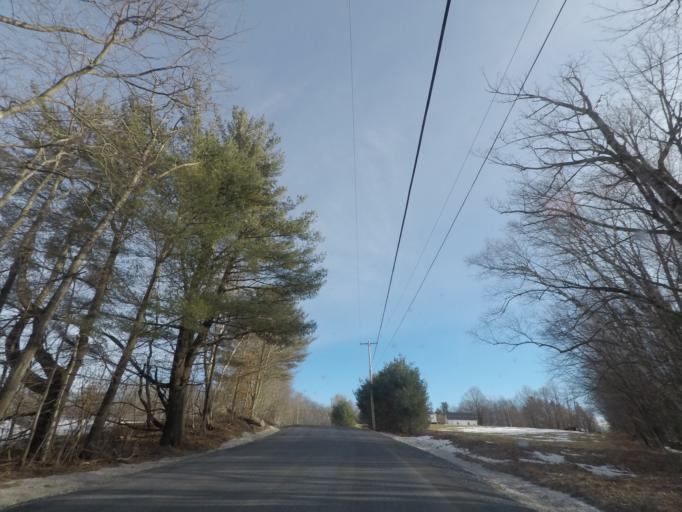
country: US
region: New York
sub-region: Rensselaer County
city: Poestenkill
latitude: 42.7605
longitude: -73.4236
